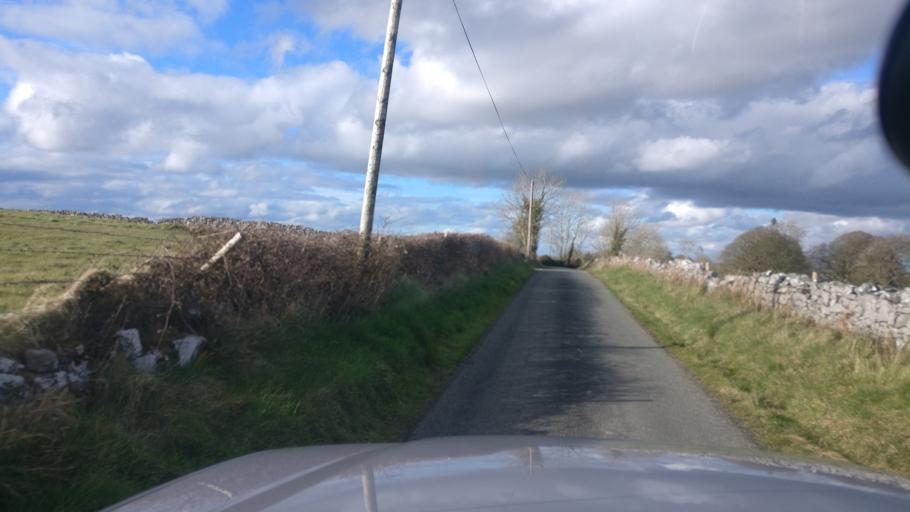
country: IE
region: Connaught
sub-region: County Galway
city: Loughrea
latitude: 53.1729
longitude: -8.4270
